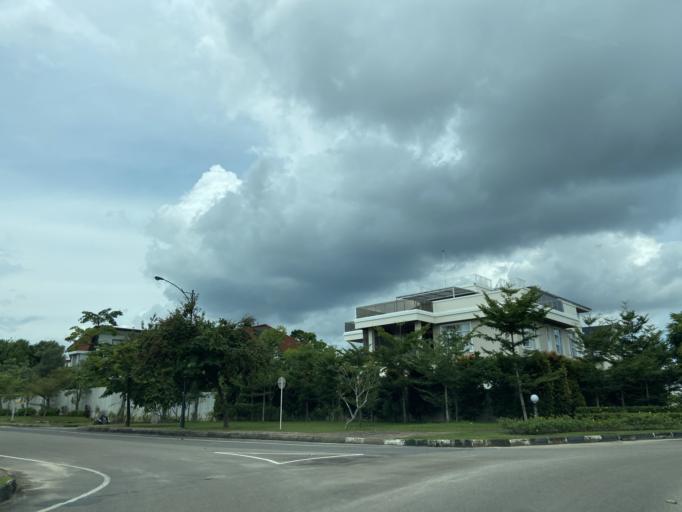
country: SG
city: Singapore
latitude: 1.1297
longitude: 103.9993
